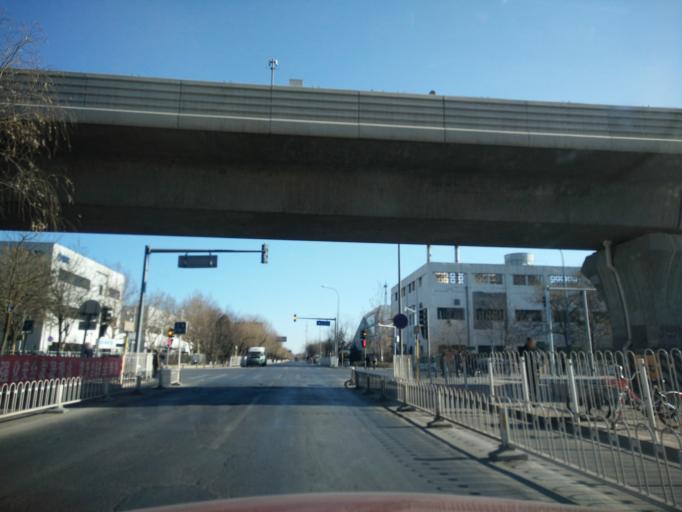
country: CN
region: Beijing
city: Jiugong
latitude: 39.8025
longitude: 116.4986
